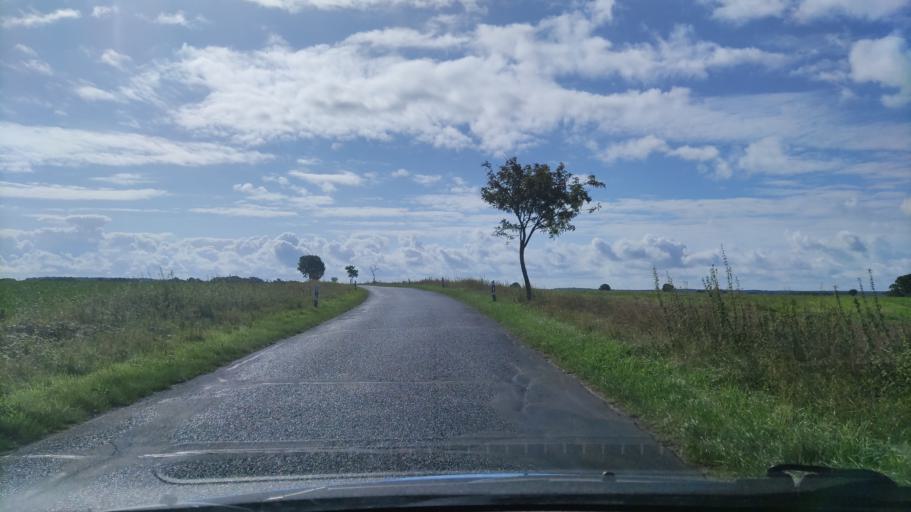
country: DE
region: Lower Saxony
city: Romstedt
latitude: 53.0855
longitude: 10.6629
